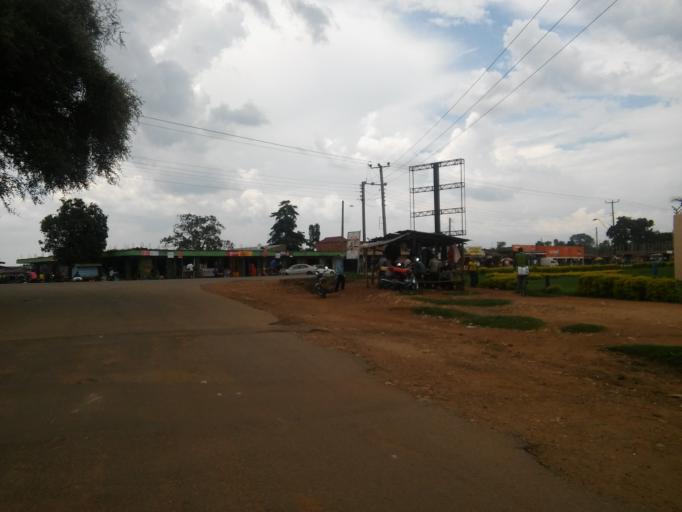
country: UG
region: Eastern Region
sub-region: Mbale District
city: Mbale
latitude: 1.0792
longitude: 34.1612
